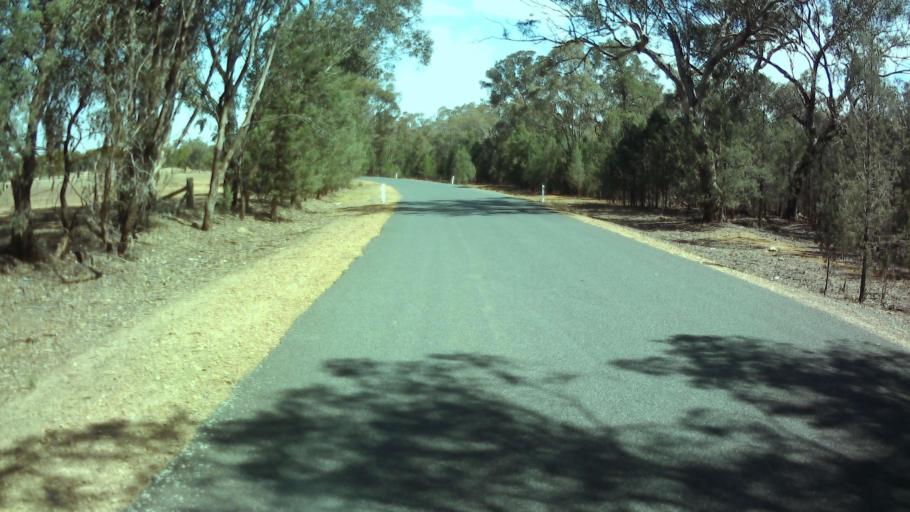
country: AU
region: New South Wales
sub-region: Weddin
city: Grenfell
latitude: -34.0220
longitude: 148.1304
